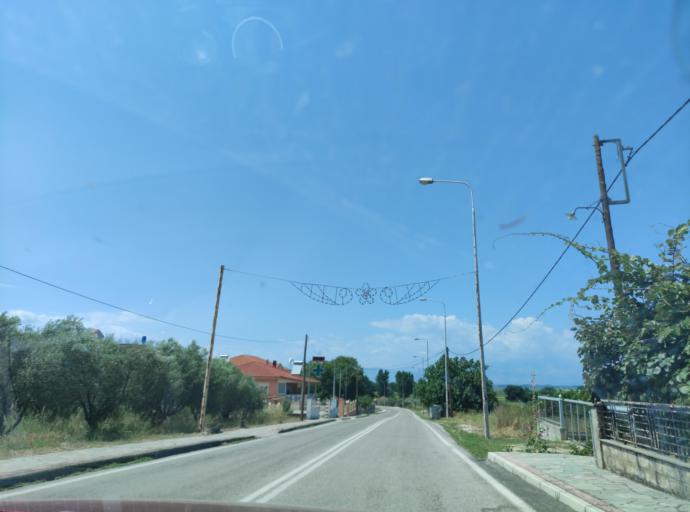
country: GR
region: East Macedonia and Thrace
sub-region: Nomos Kavalas
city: Palaiochori
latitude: 40.9476
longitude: 24.2091
